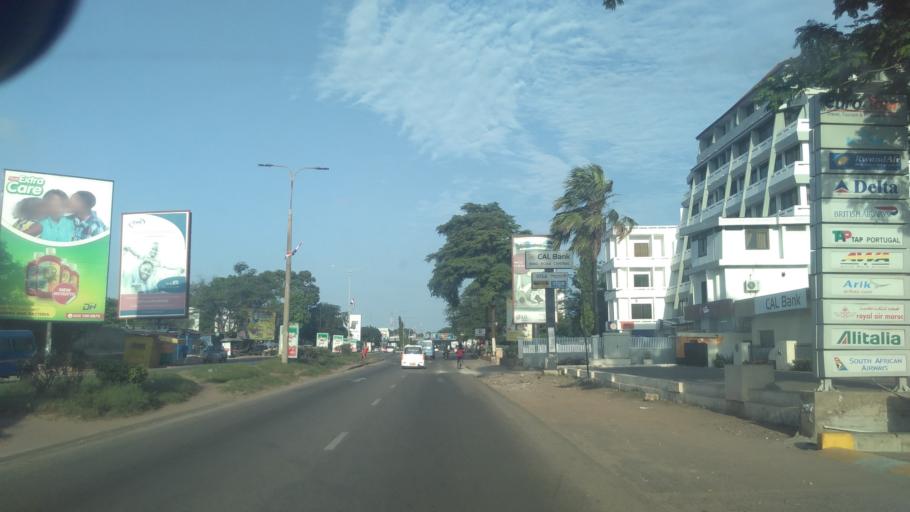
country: GH
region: Greater Accra
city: Accra
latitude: 5.5728
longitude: -0.2022
